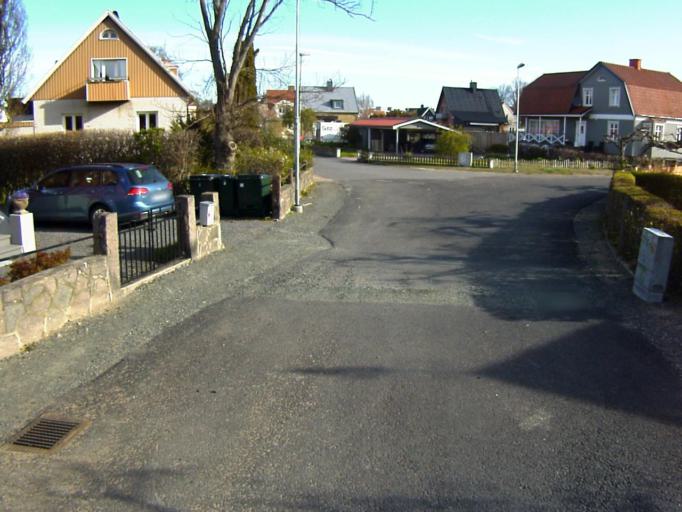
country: SE
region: Skane
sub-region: Kristianstads Kommun
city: Kristianstad
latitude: 56.0141
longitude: 14.1480
